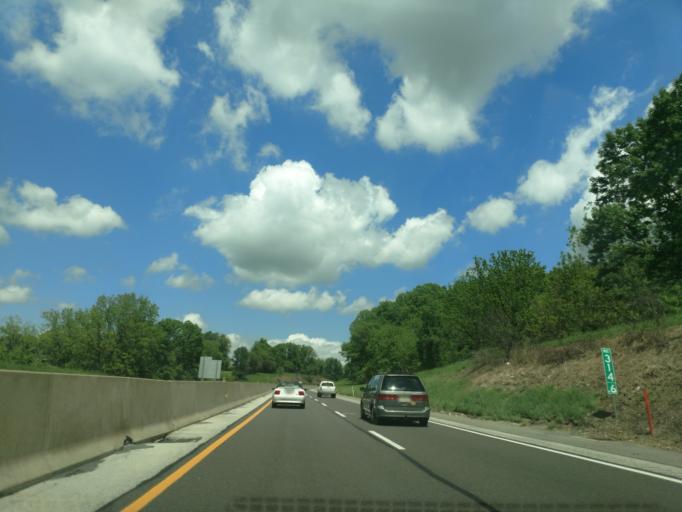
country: US
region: Pennsylvania
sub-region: Chester County
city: Chester Springs
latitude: 40.0629
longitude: -75.6210
